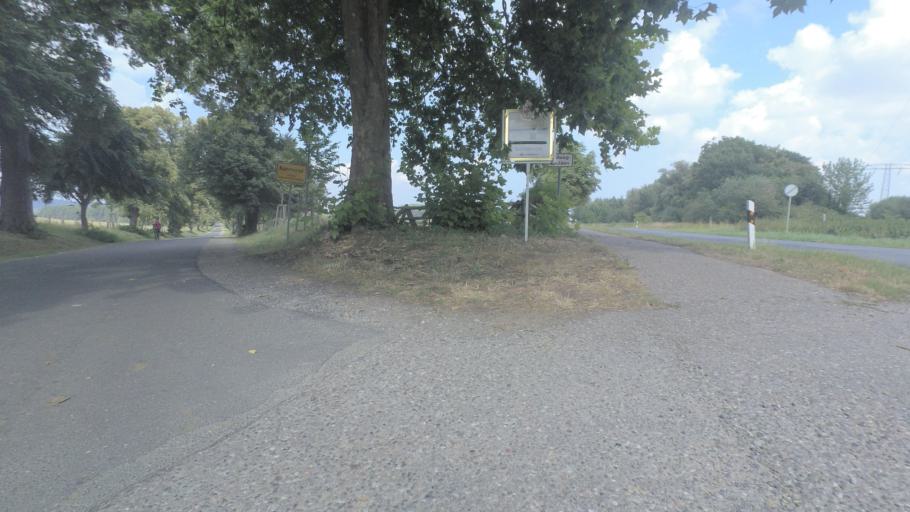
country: DE
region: Mecklenburg-Vorpommern
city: Malchin
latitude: 53.7582
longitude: 12.8375
